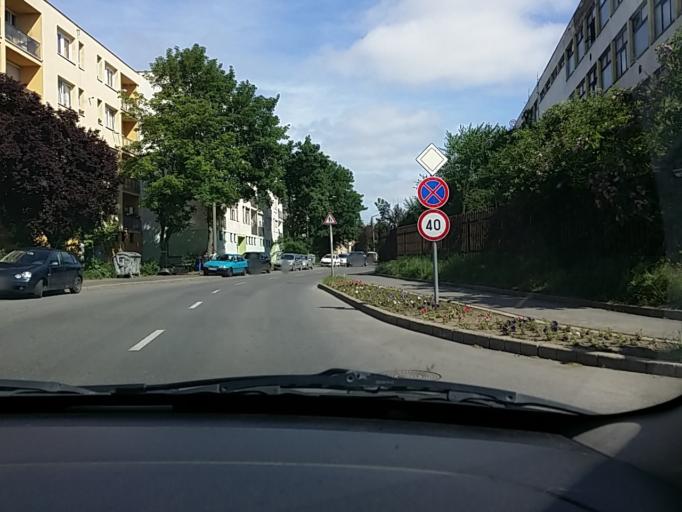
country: HU
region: Borsod-Abauj-Zemplen
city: Satoraljaujhely
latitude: 48.3959
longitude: 21.6597
